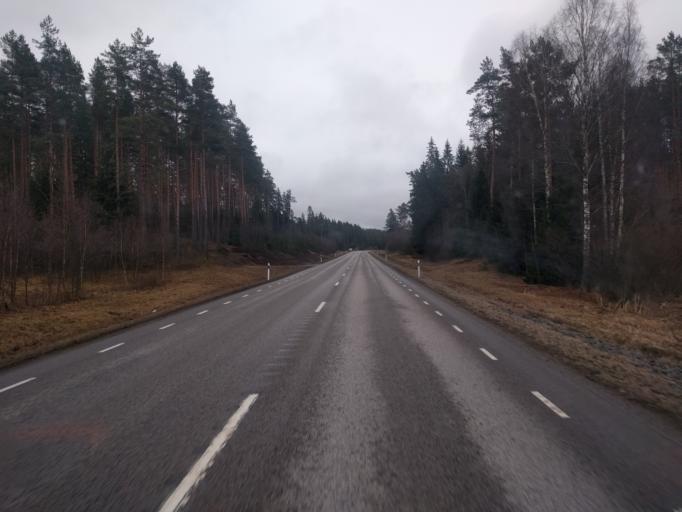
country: SE
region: Joenkoeping
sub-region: Aneby Kommun
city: Aneby
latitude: 57.7693
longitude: 14.8977
